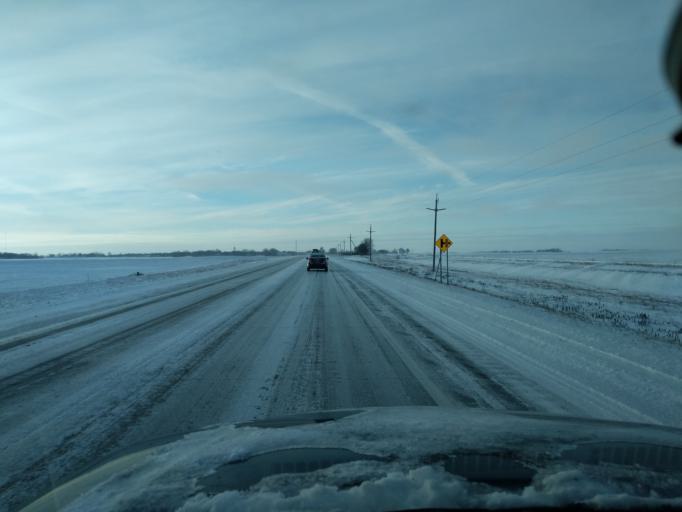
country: US
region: Minnesota
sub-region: Renville County
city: Bird Island
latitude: 44.7634
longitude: -94.8587
